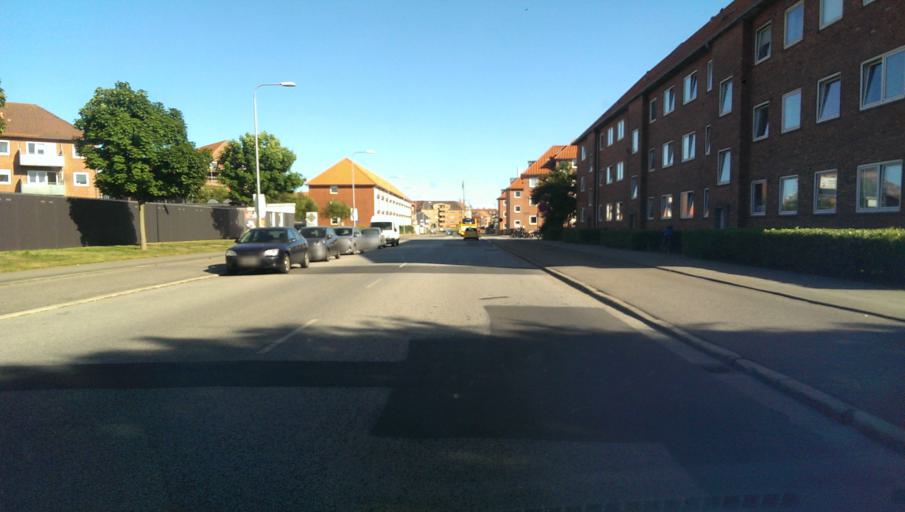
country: DK
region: South Denmark
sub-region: Esbjerg Kommune
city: Esbjerg
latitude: 55.4765
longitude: 8.4329
